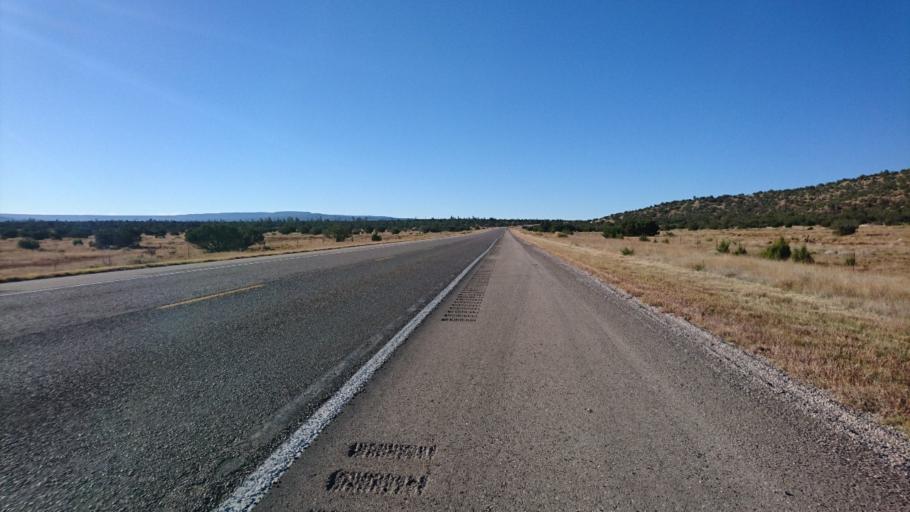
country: US
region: New Mexico
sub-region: Cibola County
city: Grants
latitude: 34.9718
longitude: -107.9125
